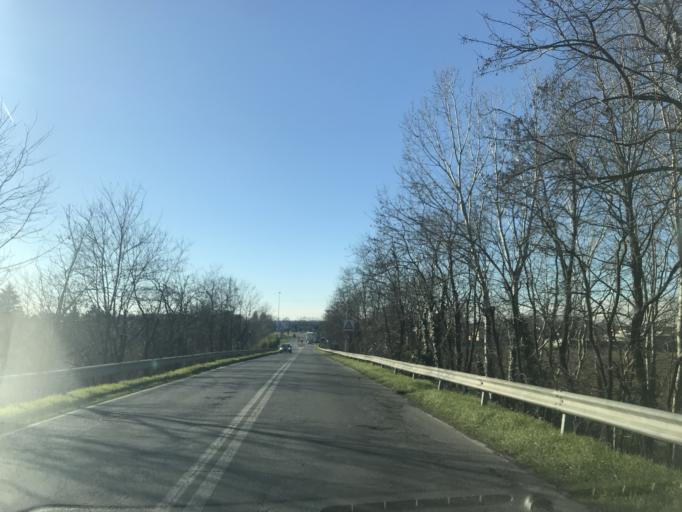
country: IT
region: Lombardy
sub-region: Provincia di Lodi
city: San Martino in Strada
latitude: 45.2775
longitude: 9.5289
